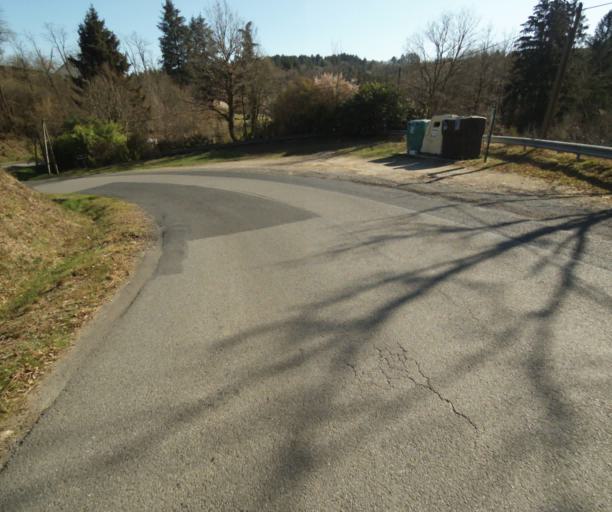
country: FR
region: Limousin
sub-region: Departement de la Correze
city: Tulle
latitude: 45.2900
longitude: 1.7252
